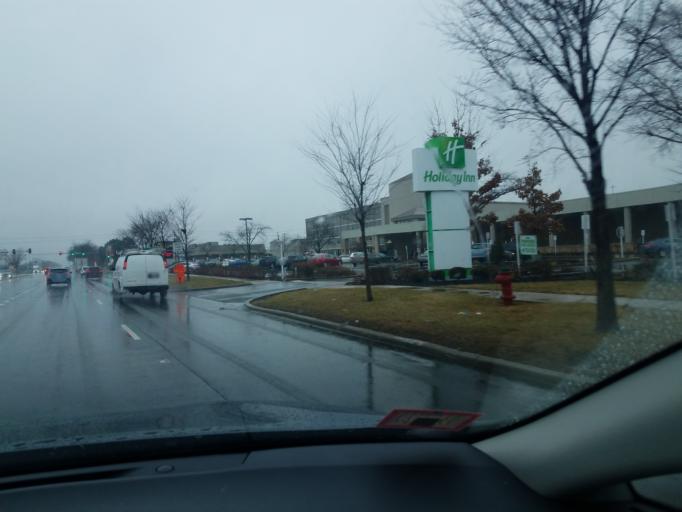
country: US
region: Illinois
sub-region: Cook County
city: Lincolnwood
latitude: 42.0120
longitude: -87.7594
